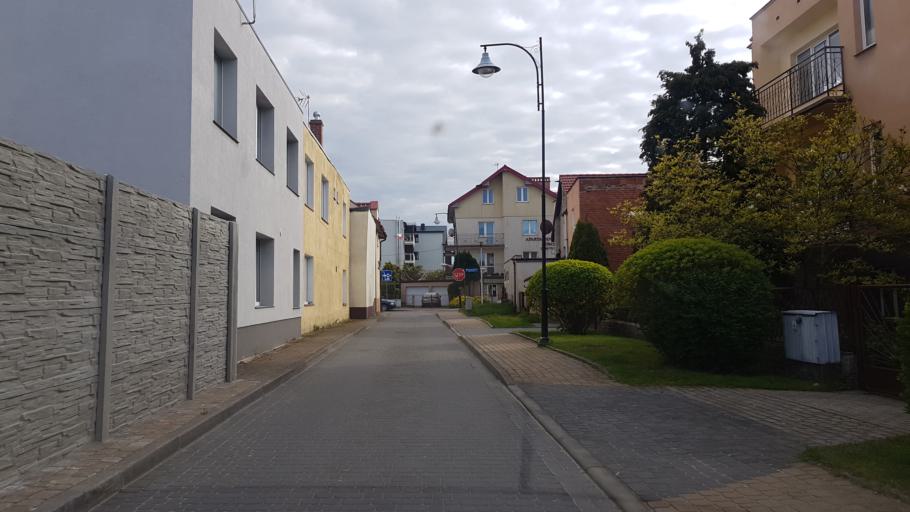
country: PL
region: West Pomeranian Voivodeship
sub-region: Powiat slawienski
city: Darlowo
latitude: 54.4379
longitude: 16.3787
